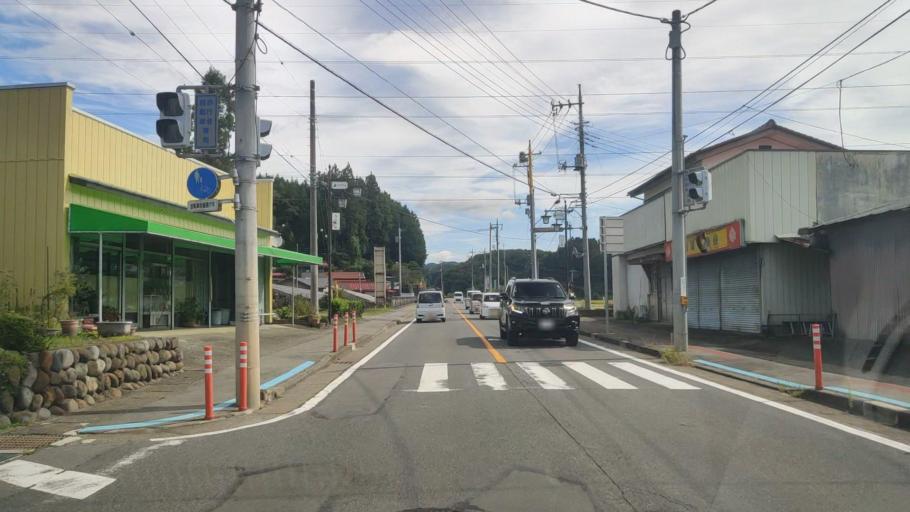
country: JP
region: Gunma
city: Numata
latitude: 36.6238
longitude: 138.9489
